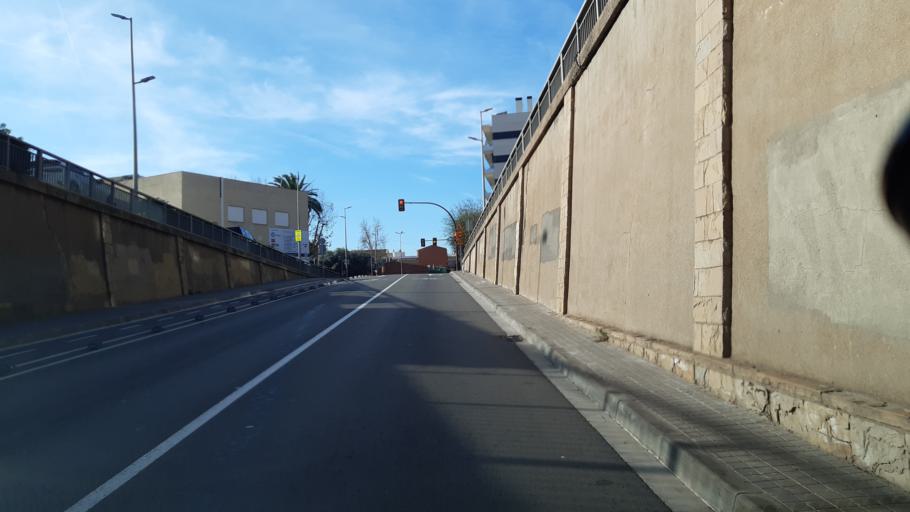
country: ES
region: Catalonia
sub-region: Provincia de Barcelona
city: L'Hospitalet de Llobregat
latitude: 41.3643
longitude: 2.1151
